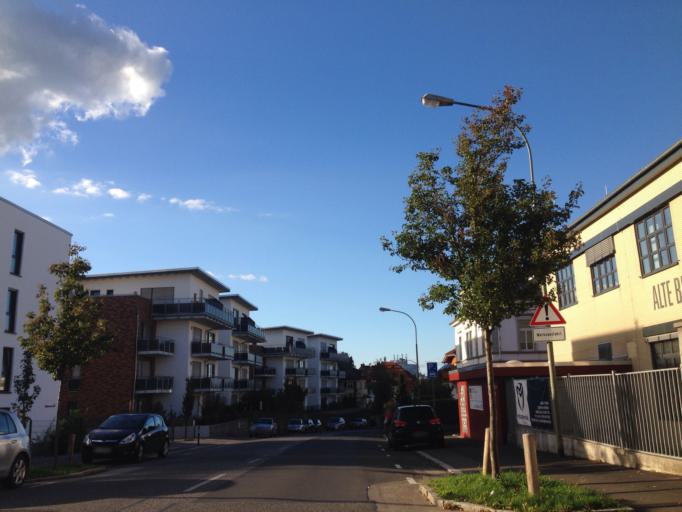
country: DE
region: Hesse
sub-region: Regierungsbezirk Giessen
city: Giessen
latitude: 50.5745
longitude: 8.6716
